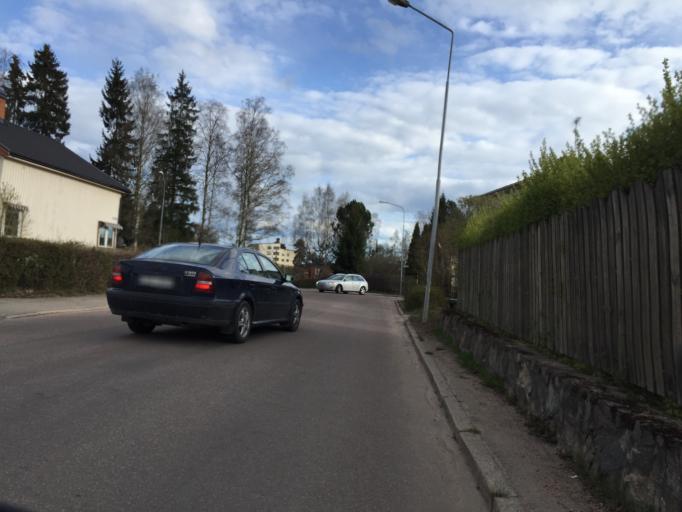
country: SE
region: Dalarna
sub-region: Ludvika Kommun
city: Ludvika
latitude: 60.1359
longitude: 15.1813
